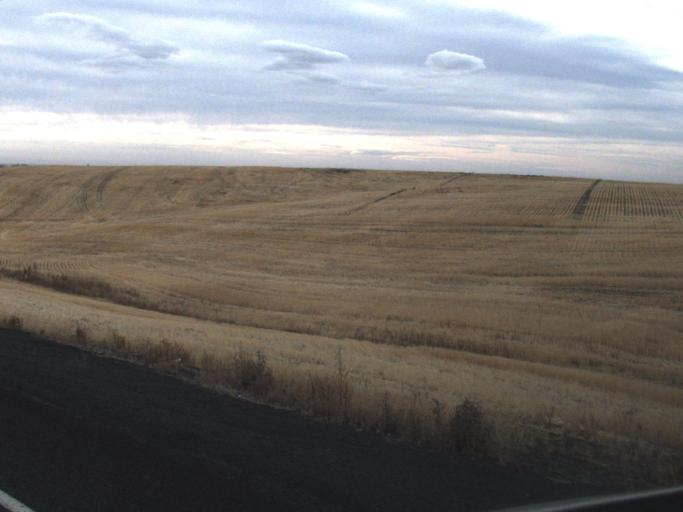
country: US
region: Washington
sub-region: Okanogan County
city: Coulee Dam
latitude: 47.8638
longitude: -118.8306
